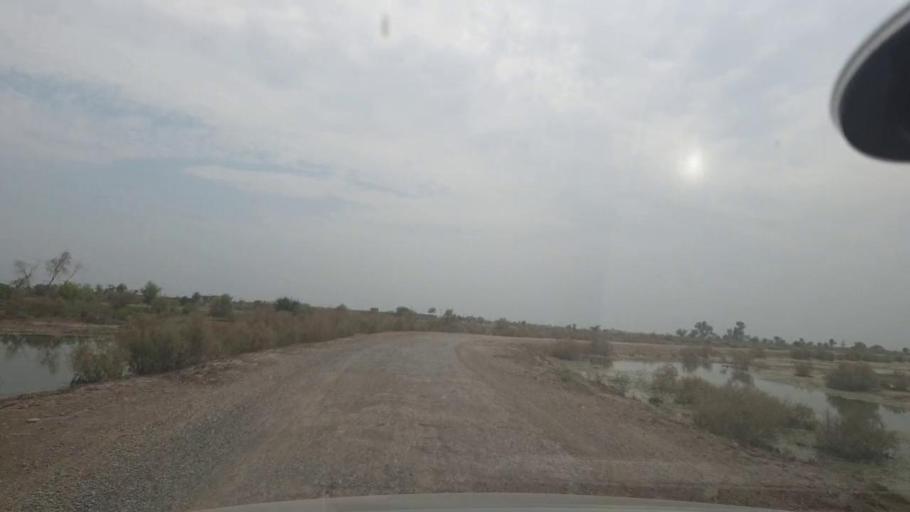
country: PK
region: Balochistan
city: Mehrabpur
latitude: 28.0553
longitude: 68.1376
